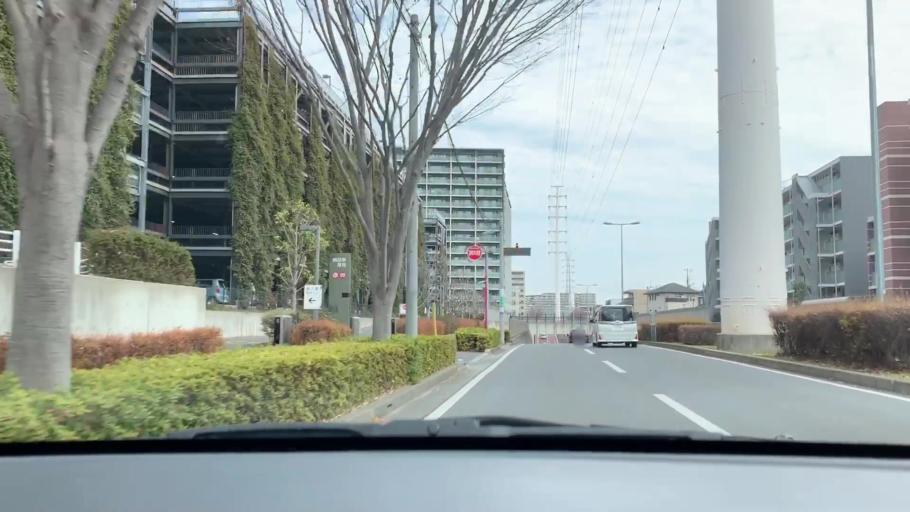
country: JP
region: Chiba
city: Nagareyama
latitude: 35.8699
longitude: 139.9268
